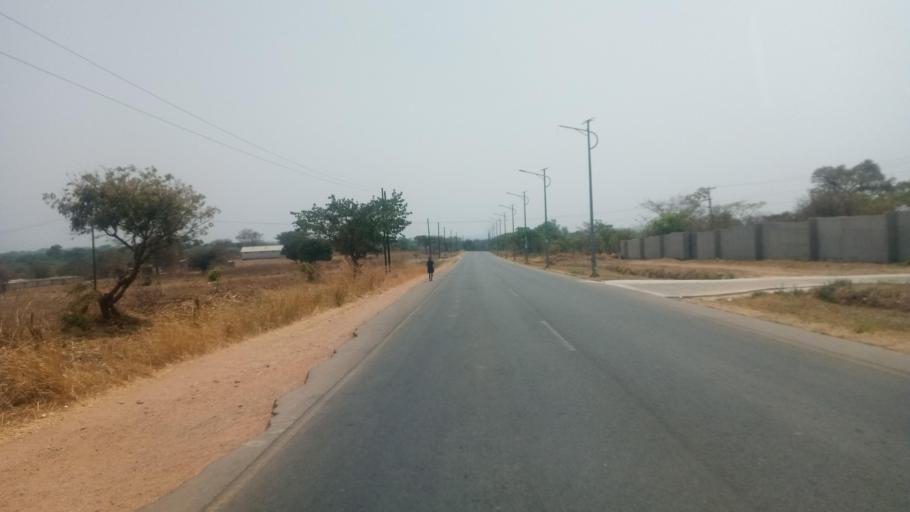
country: ZM
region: Lusaka
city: Lusaka
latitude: -15.4651
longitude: 28.4323
